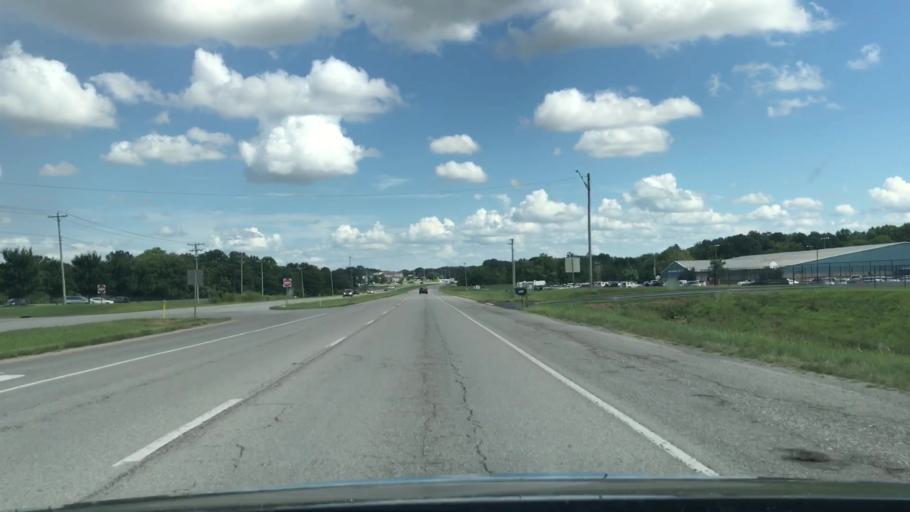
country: US
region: Kentucky
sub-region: Christian County
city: Hopkinsville
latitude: 36.8280
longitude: -87.5152
